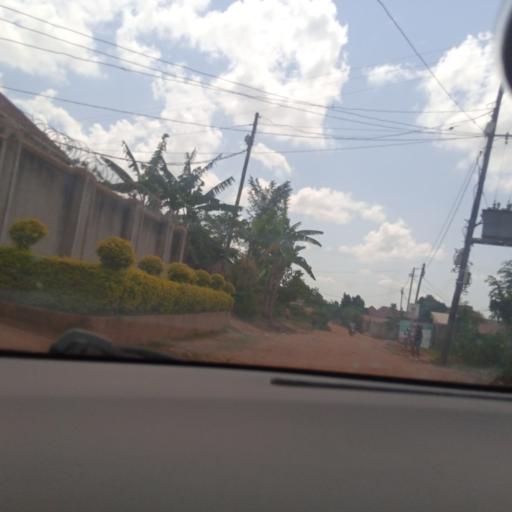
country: UG
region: Central Region
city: Masaka
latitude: -0.3273
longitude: 31.7419
